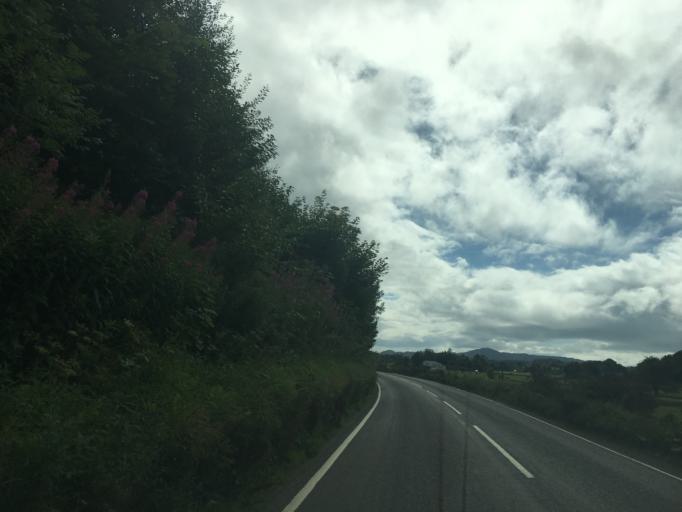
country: GB
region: Scotland
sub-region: Argyll and Bute
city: Lochgilphead
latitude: 56.1307
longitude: -5.4850
